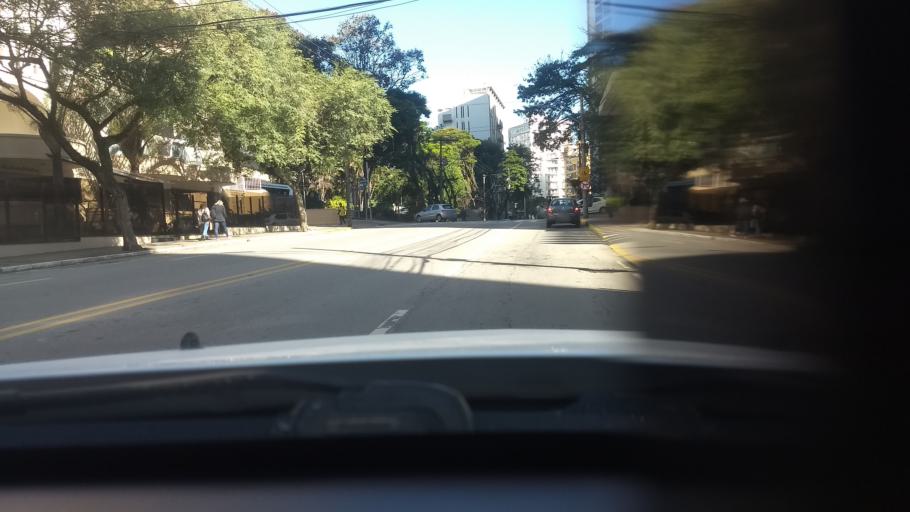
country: BR
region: Santa Catarina
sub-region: Florianopolis
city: Florianopolis
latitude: -27.5883
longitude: -48.5513
